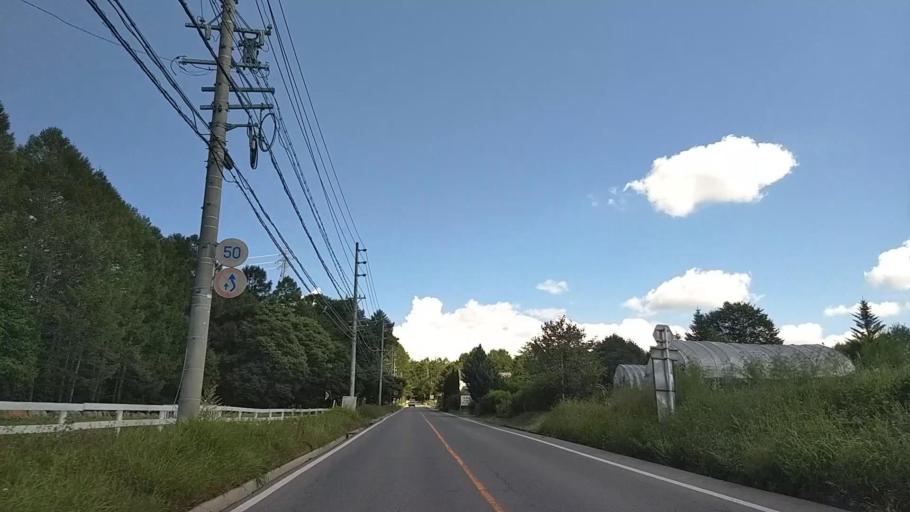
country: JP
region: Nagano
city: Chino
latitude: 36.0355
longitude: 138.2333
